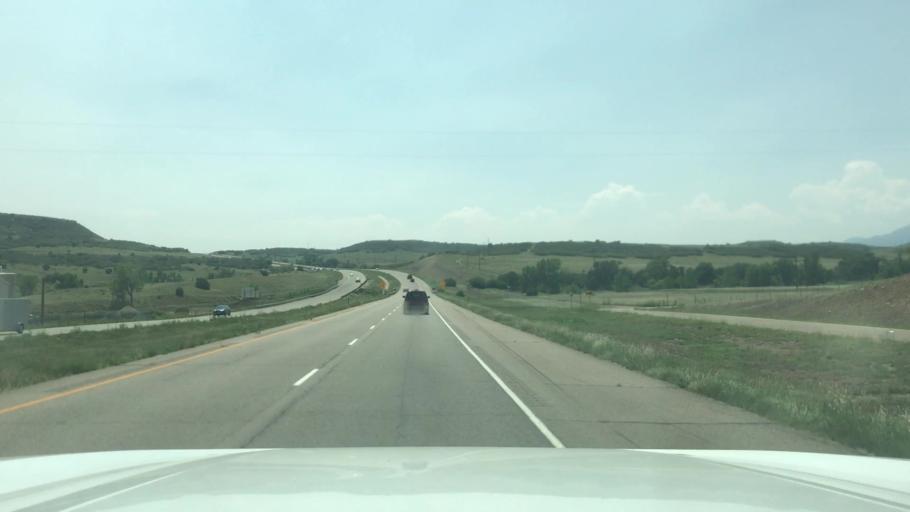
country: US
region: Colorado
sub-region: Pueblo County
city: Colorado City
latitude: 37.9159
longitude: -104.8267
